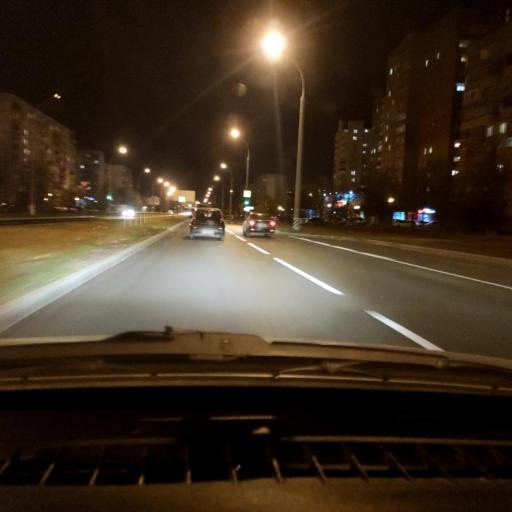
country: RU
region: Samara
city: Tol'yatti
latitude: 53.5439
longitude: 49.3312
